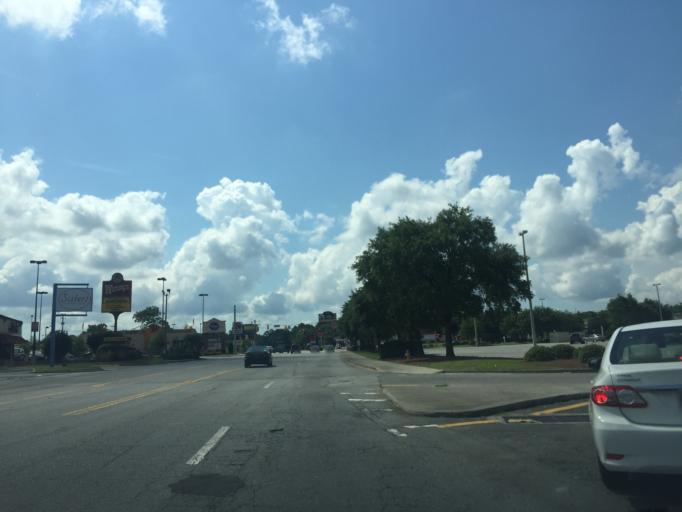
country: US
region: Georgia
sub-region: Chatham County
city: Isle of Hope
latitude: 32.0055
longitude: -81.1152
